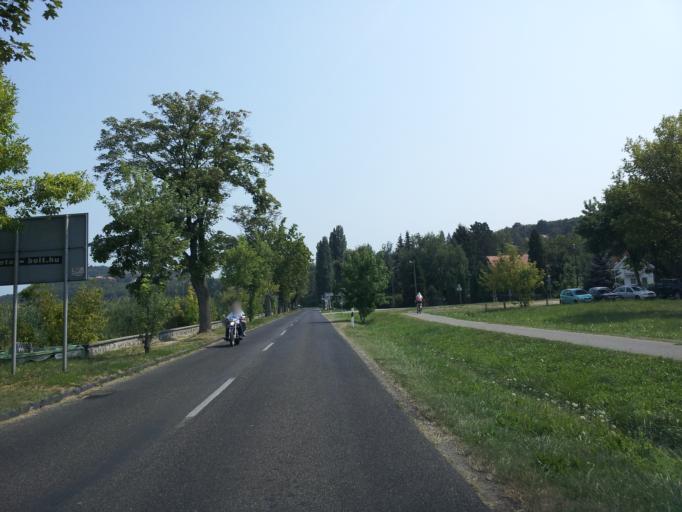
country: HU
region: Veszprem
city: Tihany
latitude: 46.9273
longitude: 17.8616
